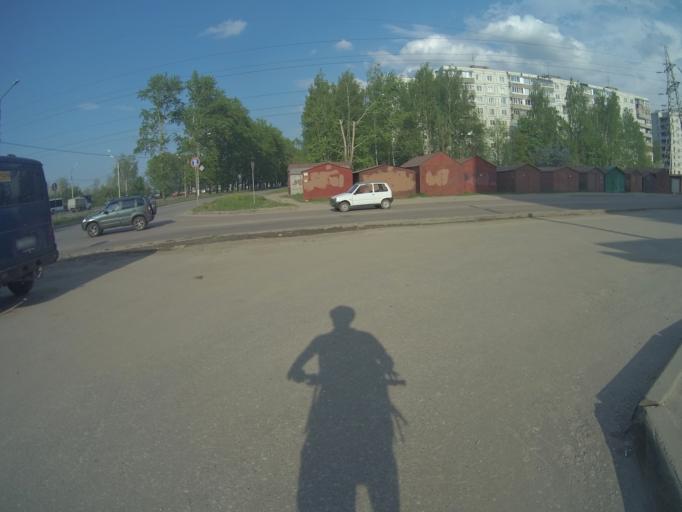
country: RU
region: Vladimir
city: Kommunar
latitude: 56.1729
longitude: 40.4521
